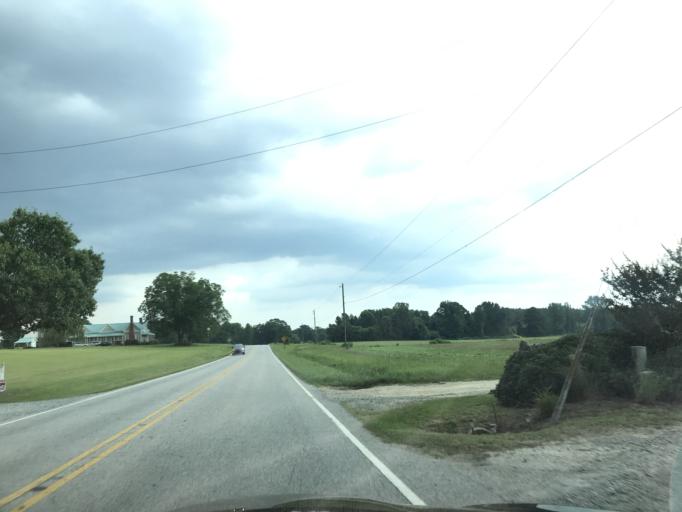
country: US
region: North Carolina
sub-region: Johnston County
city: Four Oaks
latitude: 35.5112
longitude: -78.4779
